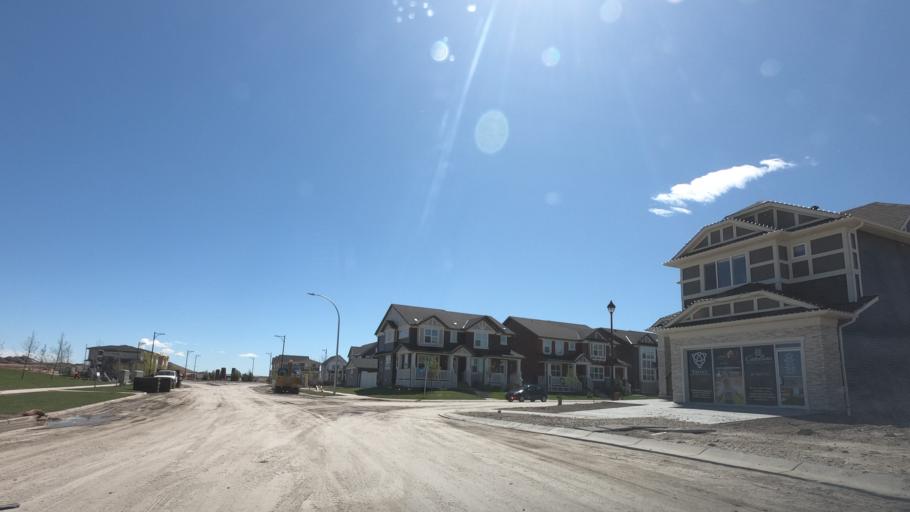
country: CA
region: Alberta
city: Airdrie
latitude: 51.2590
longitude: -113.9833
